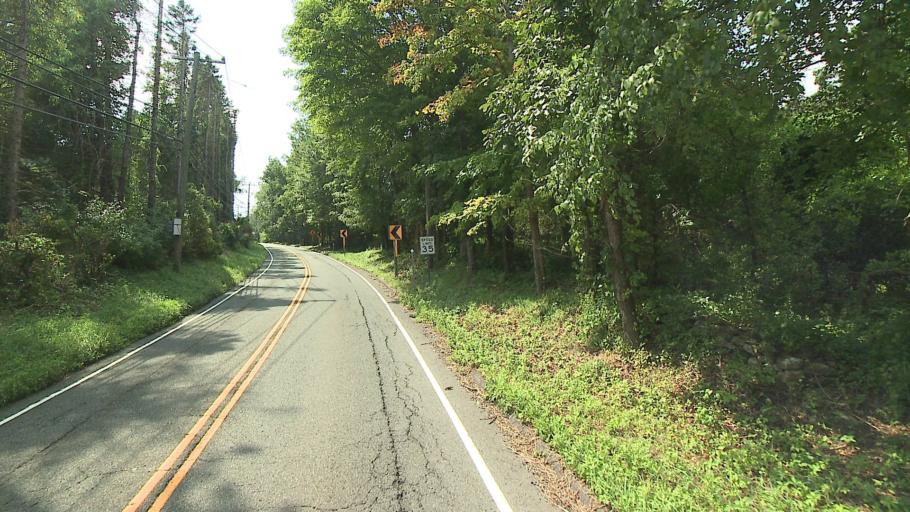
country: US
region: Connecticut
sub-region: Litchfield County
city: New Preston
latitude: 41.6428
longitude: -73.3334
